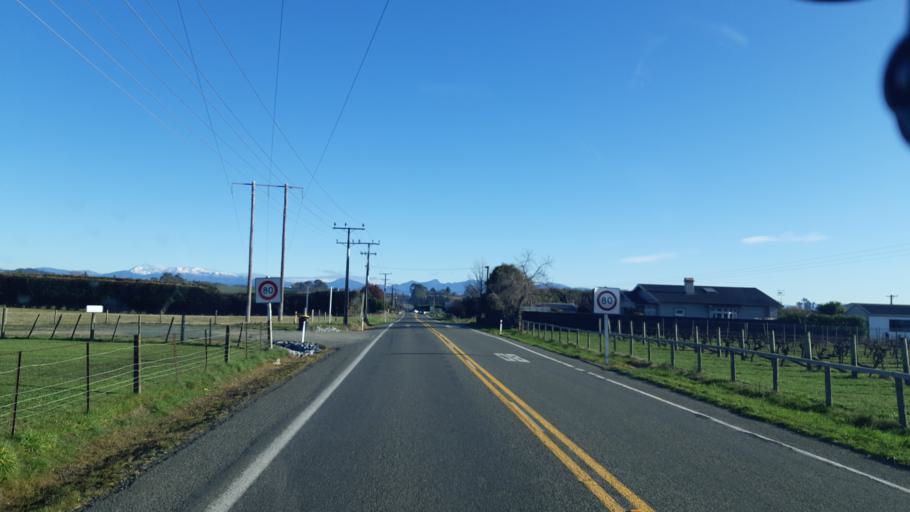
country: NZ
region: Tasman
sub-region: Tasman District
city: Mapua
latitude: -41.3045
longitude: 173.1184
